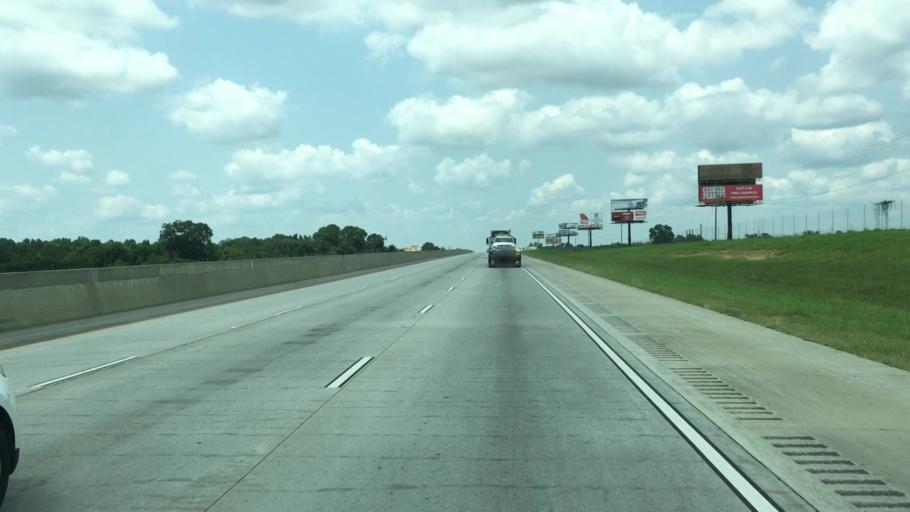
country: US
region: Georgia
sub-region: Tift County
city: Unionville
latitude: 31.3722
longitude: -83.4933
